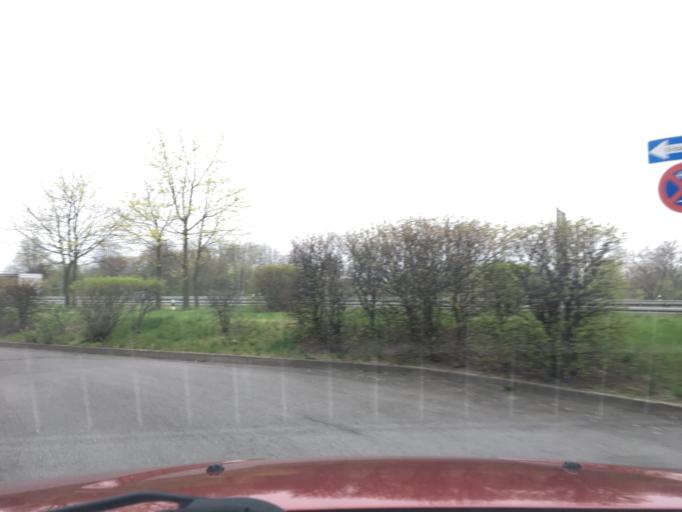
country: DE
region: Brandenburg
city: Schulzendorf
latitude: 52.3679
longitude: 13.5554
